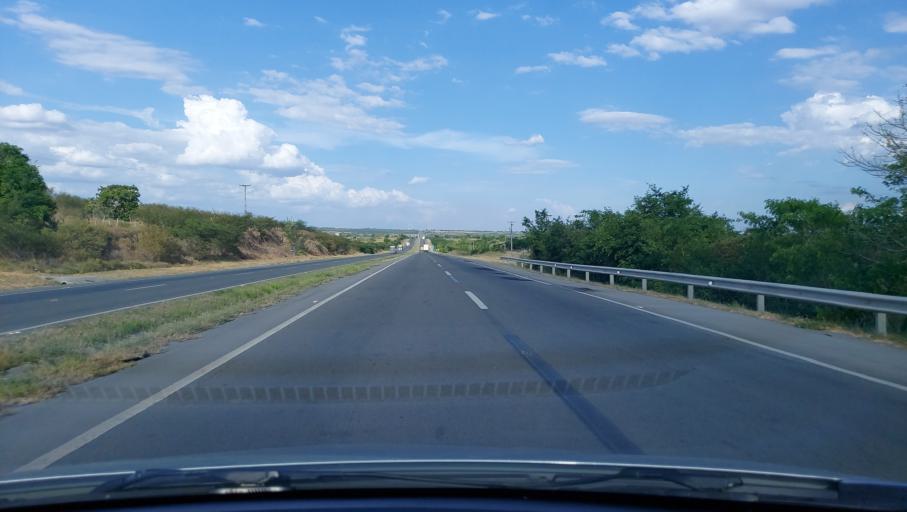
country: BR
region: Bahia
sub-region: Santo Estevao
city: Santo Estevao
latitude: -12.4884
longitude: -39.3270
